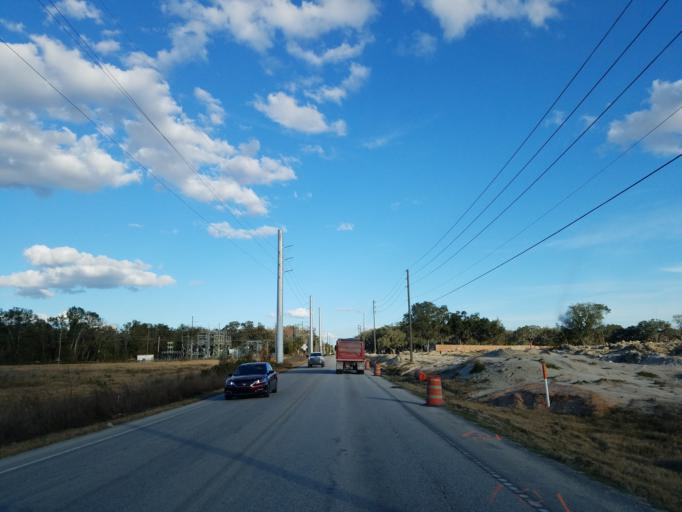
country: US
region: Florida
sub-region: Sumter County
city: Wildwood
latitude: 28.7998
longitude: -82.0453
